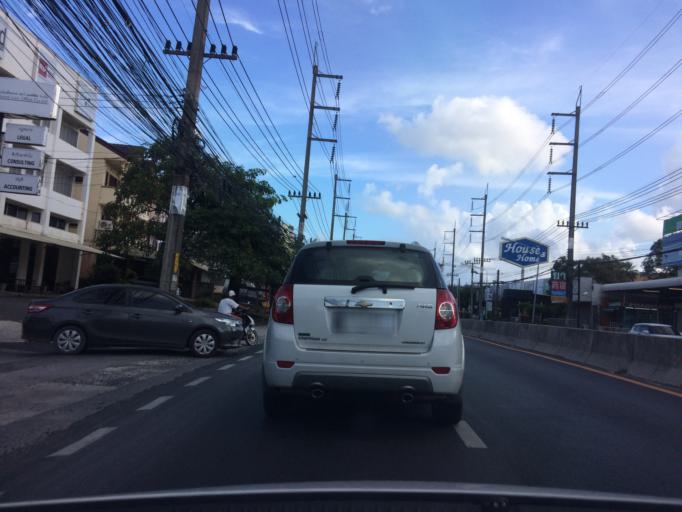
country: TH
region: Phuket
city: Mueang Phuket
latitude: 7.8771
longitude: 98.3636
